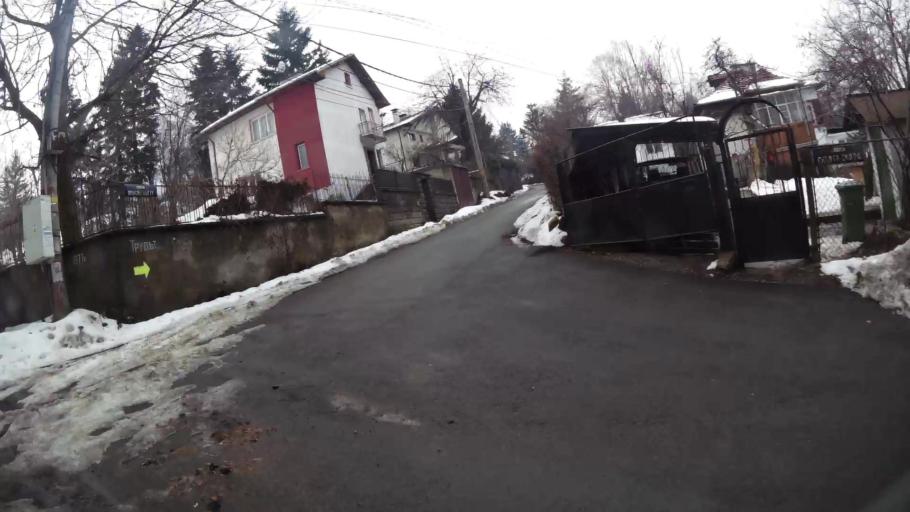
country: BG
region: Sofia-Capital
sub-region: Stolichna Obshtina
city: Sofia
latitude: 42.6531
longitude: 23.2329
